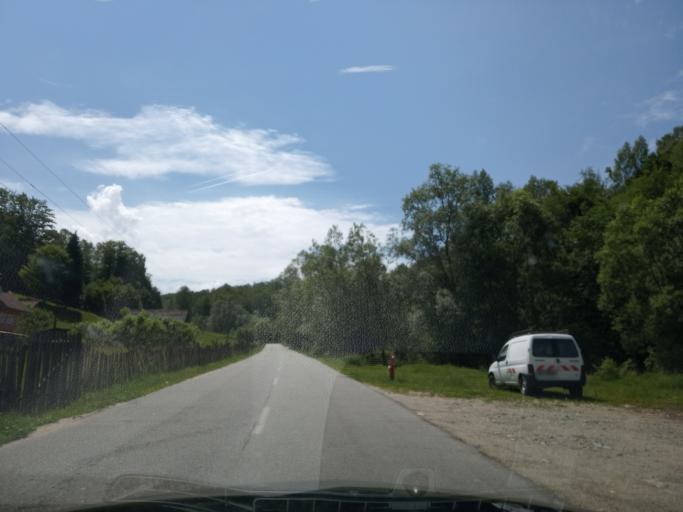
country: RO
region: Hunedoara
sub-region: Oras Petrila
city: Petrila
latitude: 45.4079
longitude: 23.4118
